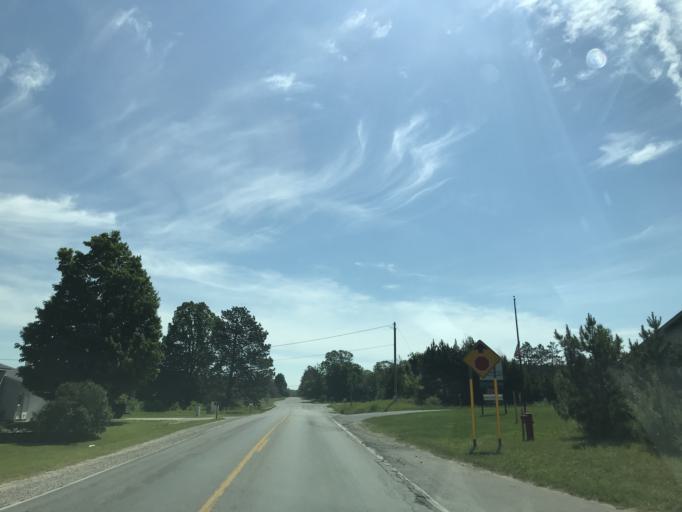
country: US
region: Michigan
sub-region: Grand Traverse County
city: Traverse City
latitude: 44.6575
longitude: -85.6590
